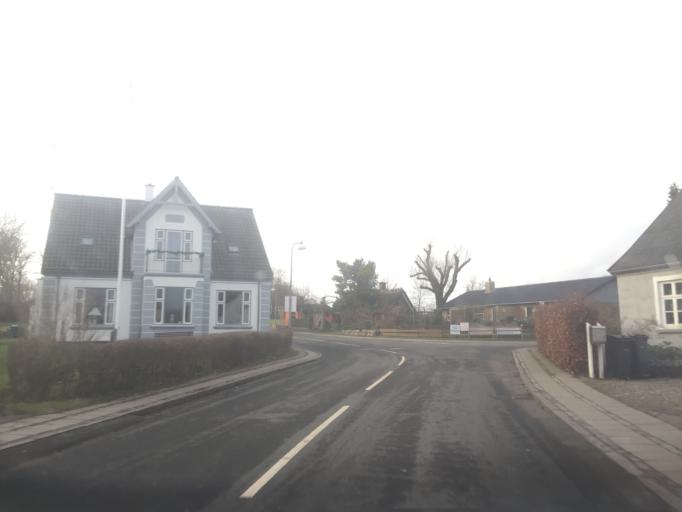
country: DK
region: Capital Region
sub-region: Egedal Kommune
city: Smorumnedre
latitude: 55.7109
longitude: 12.2984
